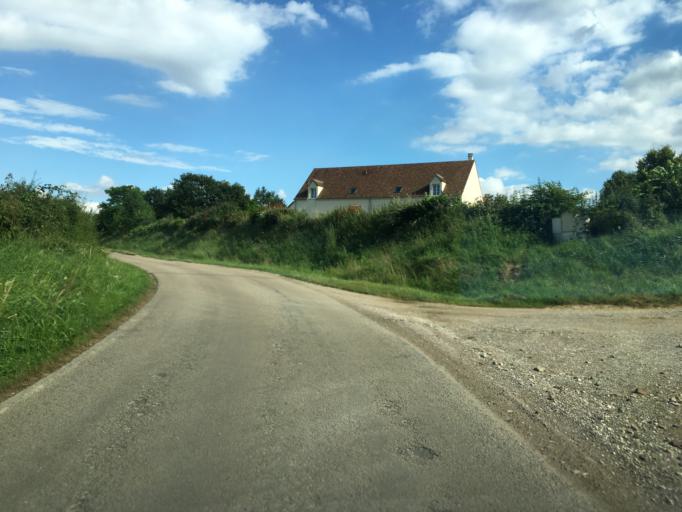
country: FR
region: Bourgogne
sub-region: Departement de l'Yonne
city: Appoigny
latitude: 47.8823
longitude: 3.5166
